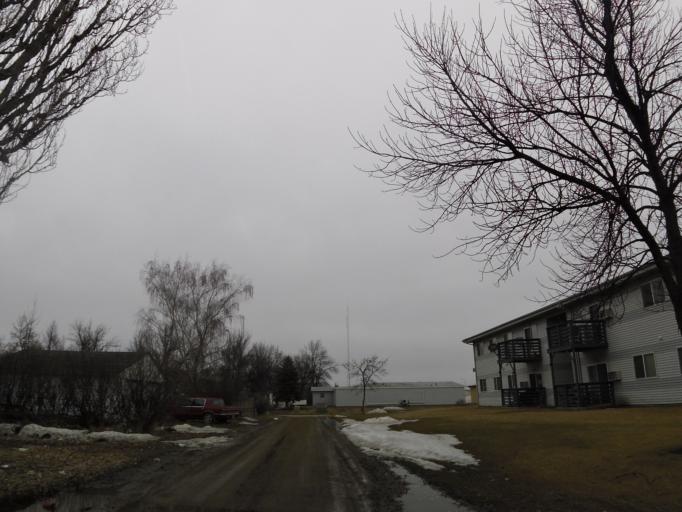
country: US
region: North Dakota
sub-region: Walsh County
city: Grafton
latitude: 48.4098
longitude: -97.4089
